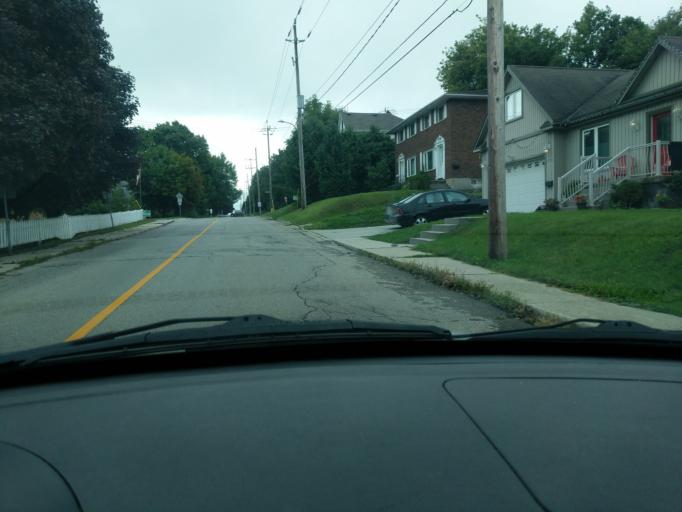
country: CA
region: Ontario
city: Cambridge
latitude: 43.4306
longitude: -80.3016
